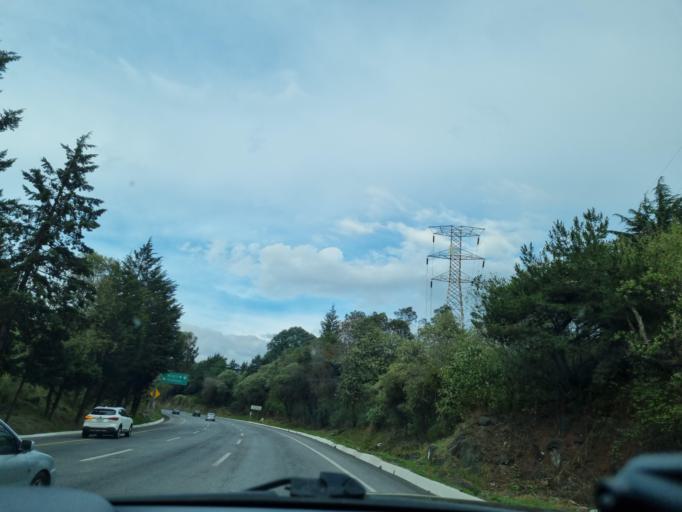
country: MX
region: Morelos
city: San Jeronimo Acazulco
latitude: 19.2884
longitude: -99.4317
